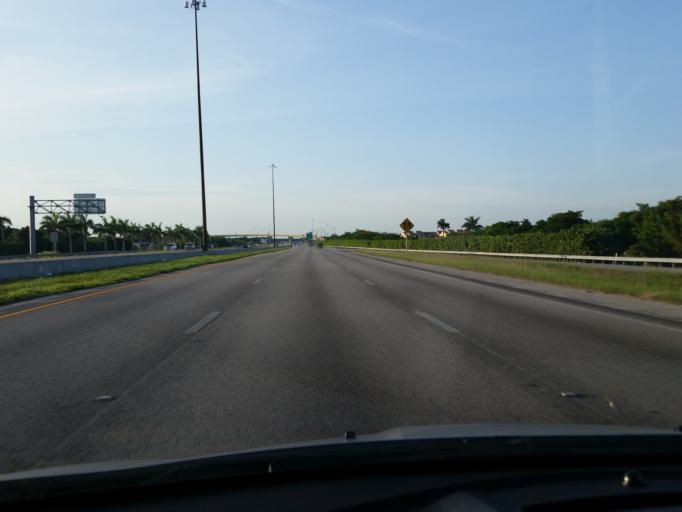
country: US
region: Florida
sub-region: Miami-Dade County
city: Lake Lucerne
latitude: 25.9618
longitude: -80.2292
